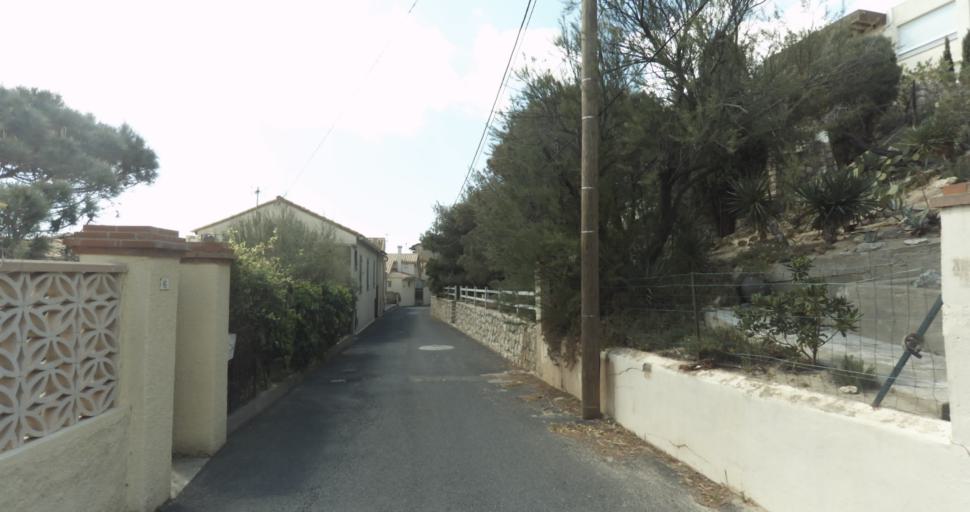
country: FR
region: Languedoc-Roussillon
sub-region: Departement de l'Aude
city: Leucate
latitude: 42.9070
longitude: 3.0564
